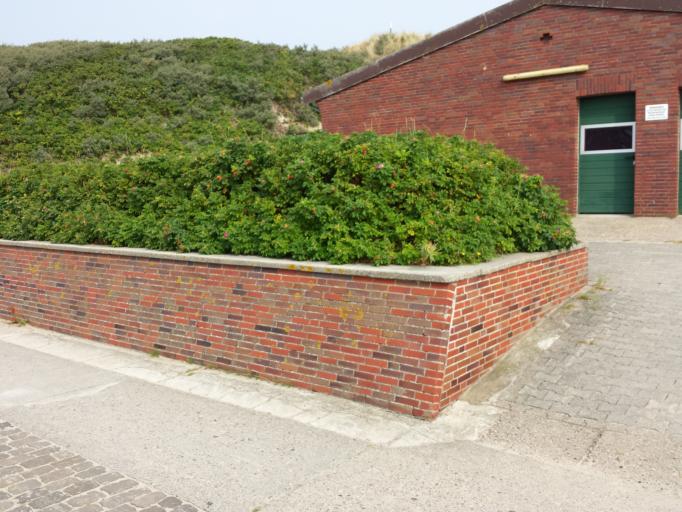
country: DE
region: Lower Saxony
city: Spiekeroog
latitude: 53.7670
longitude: 7.6723
